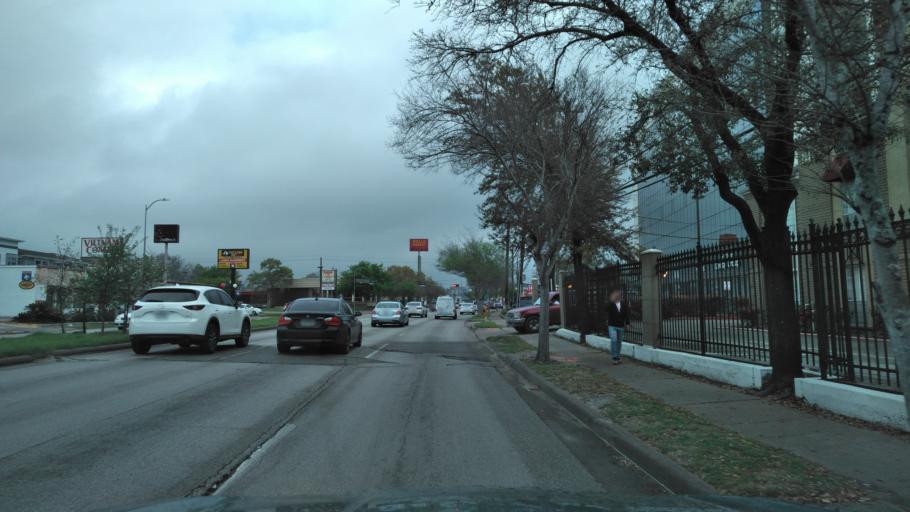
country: US
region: Texas
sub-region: Harris County
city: Piney Point Village
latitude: 29.7337
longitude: -95.5011
